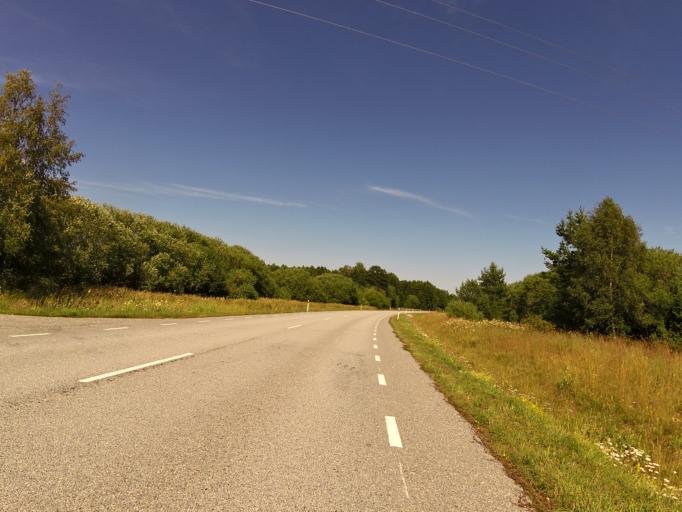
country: EE
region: Hiiumaa
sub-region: Kaerdla linn
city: Kardla
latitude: 58.9986
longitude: 22.5316
